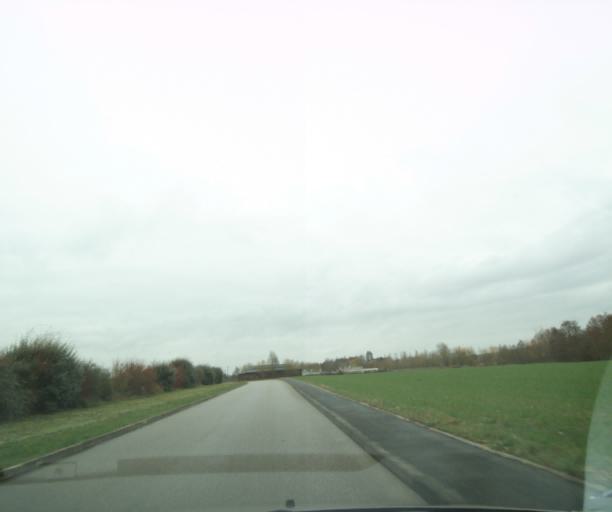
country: FR
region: Picardie
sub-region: Departement de l'Oise
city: Noyon
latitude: 49.5697
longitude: 2.9980
